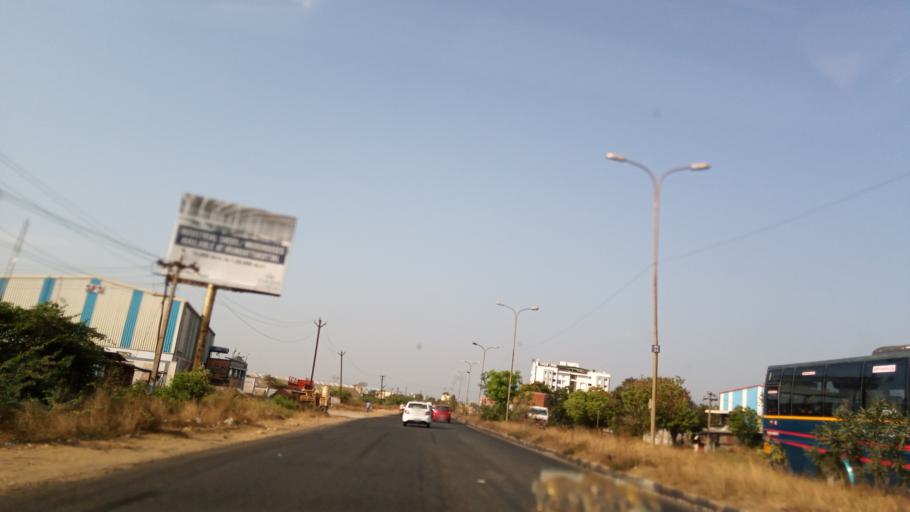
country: IN
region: Tamil Nadu
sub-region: Kancheepuram
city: Sriperumbudur
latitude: 13.0082
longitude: 79.9963
